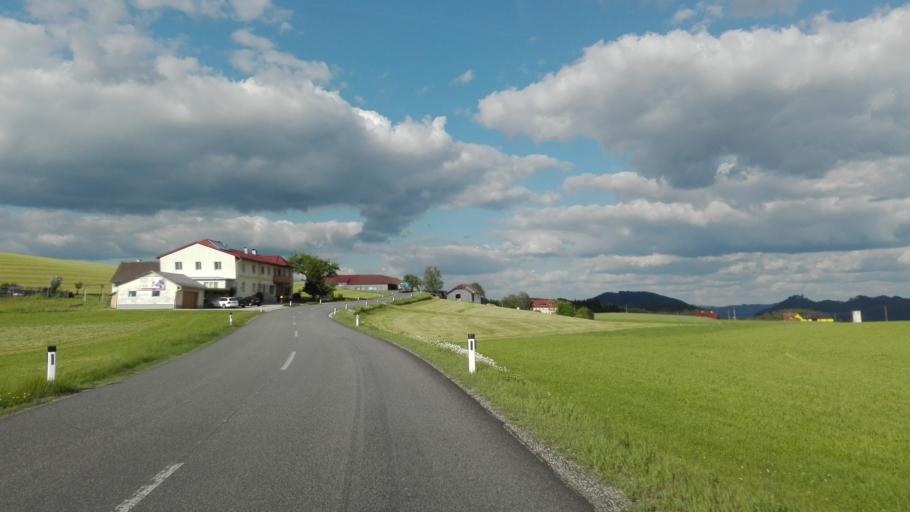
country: AT
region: Upper Austria
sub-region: Politischer Bezirk Perg
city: Perg
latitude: 48.3772
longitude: 14.6995
